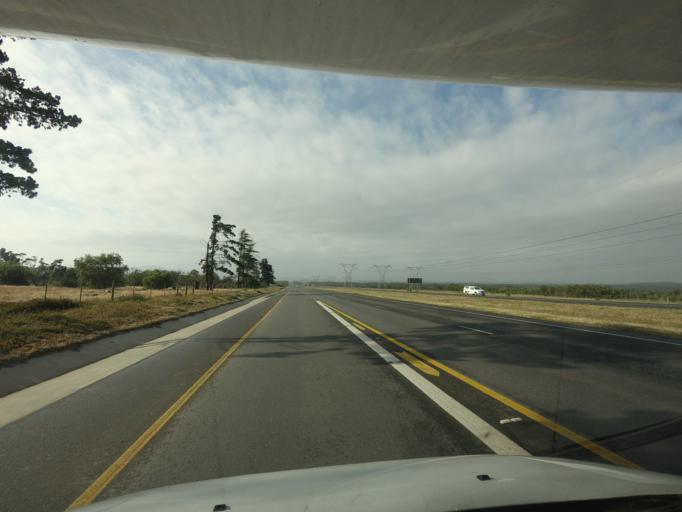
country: ZA
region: Western Cape
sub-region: City of Cape Town
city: Sunset Beach
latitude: -33.7285
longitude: 18.5449
